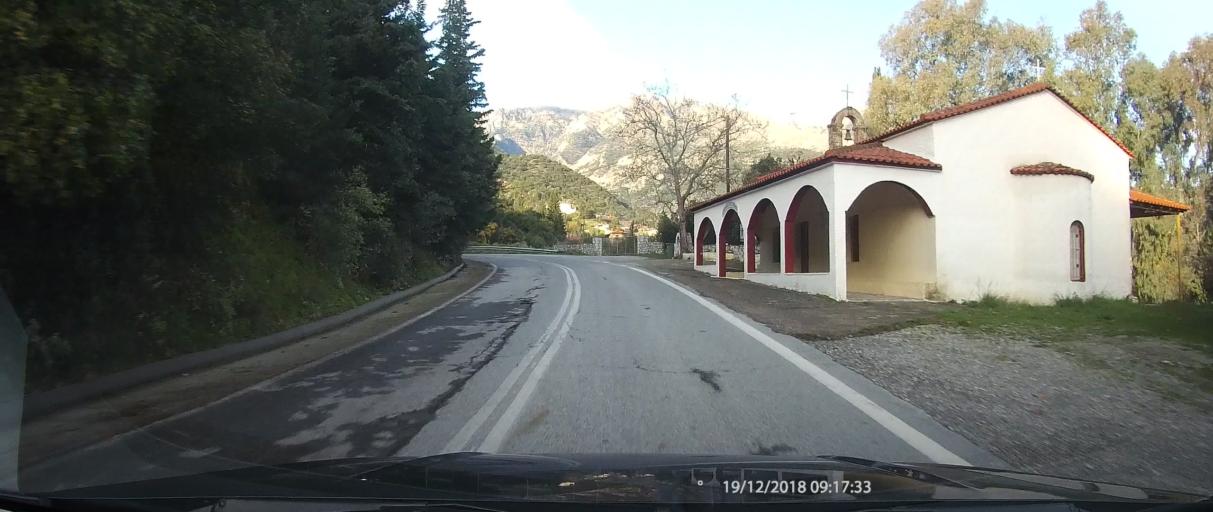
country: GR
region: Peloponnese
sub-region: Nomos Lakonias
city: Magoula
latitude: 37.0921
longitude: 22.3584
